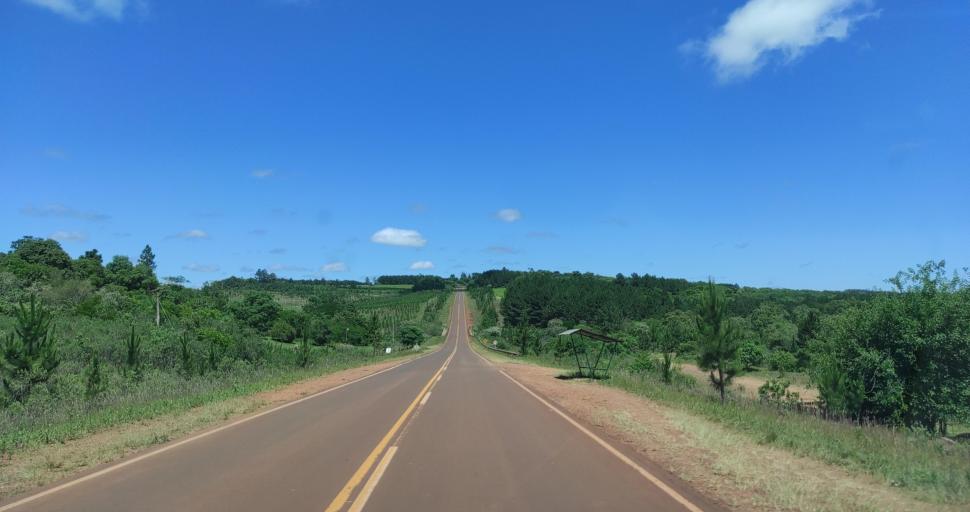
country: AR
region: Misiones
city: Campo Grande
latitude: -27.2404
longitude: -54.9145
